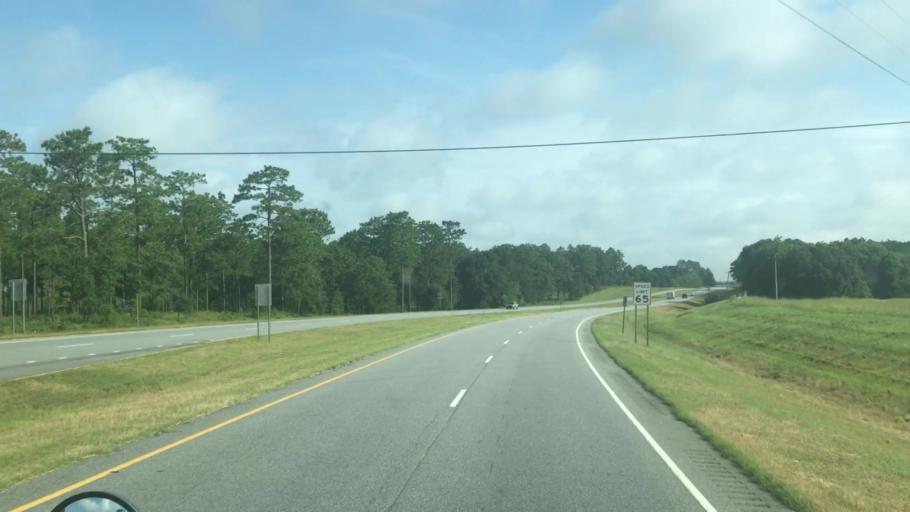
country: US
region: Georgia
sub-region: Decatur County
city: Bainbridge
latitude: 30.9478
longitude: -84.6118
